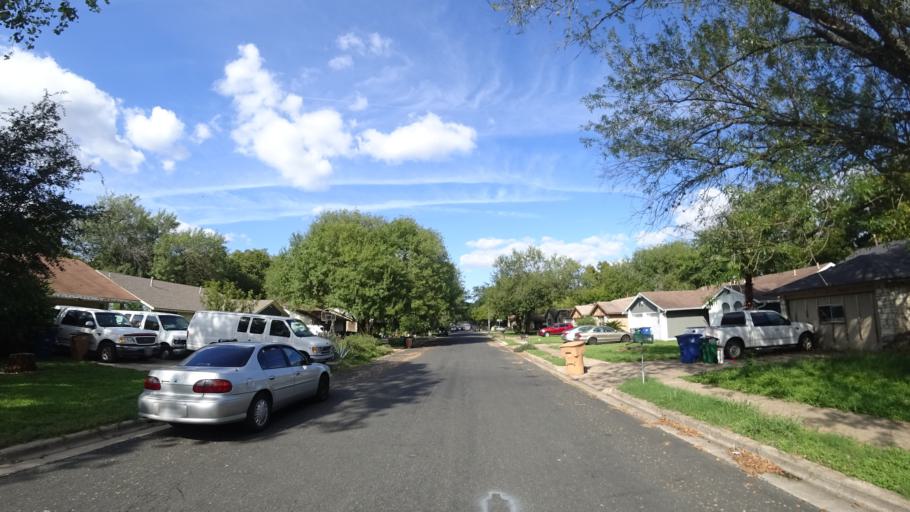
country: US
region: Texas
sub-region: Travis County
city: Rollingwood
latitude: 30.2081
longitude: -97.7966
